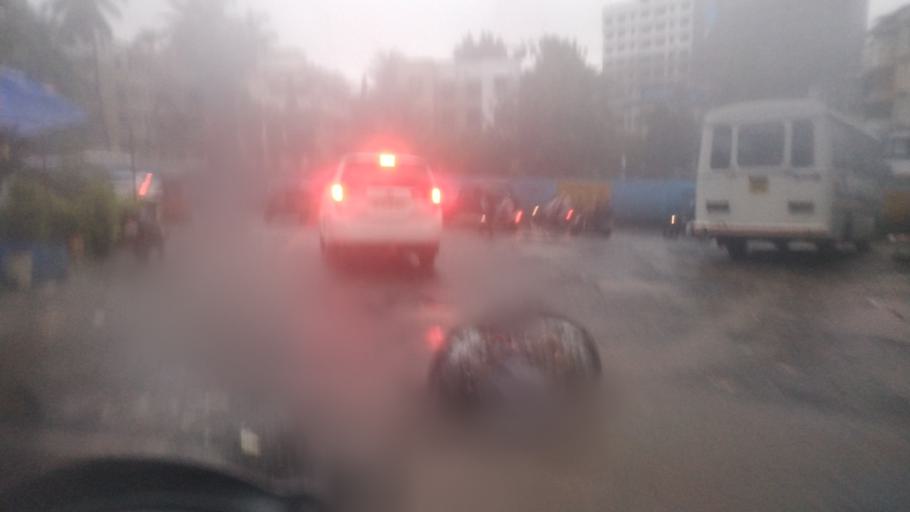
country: IN
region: Maharashtra
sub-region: Mumbai Suburban
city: Mumbai
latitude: 19.1141
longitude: 72.8534
